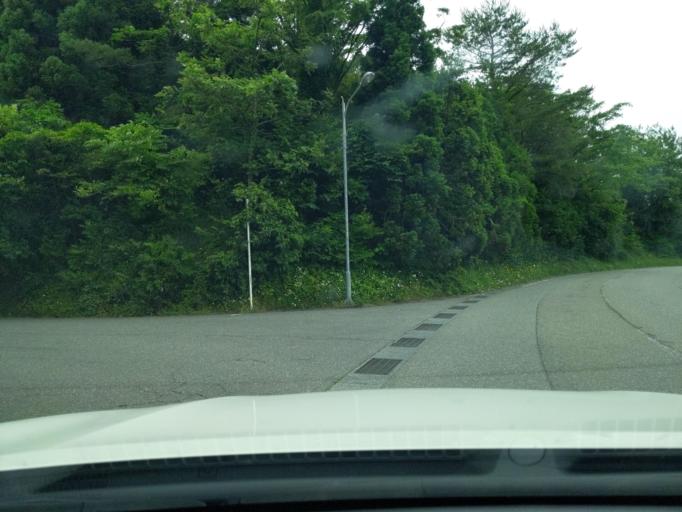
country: JP
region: Niigata
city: Kashiwazaki
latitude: 37.3416
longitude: 138.6010
